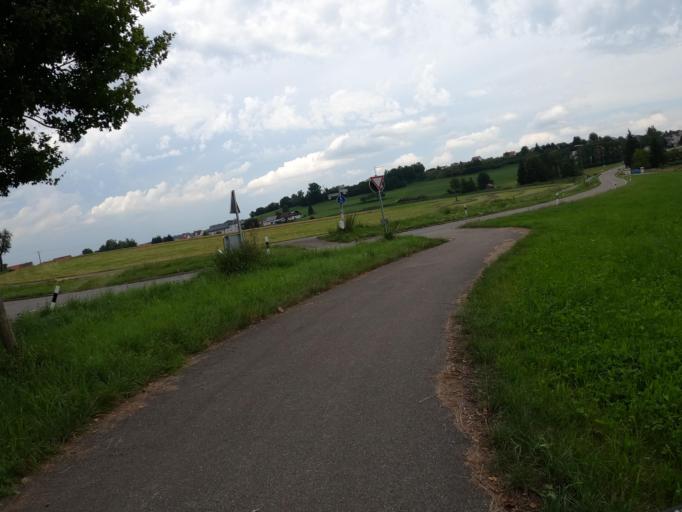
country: DE
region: Bavaria
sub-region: Swabia
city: Pfaffenhofen an der Roth
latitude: 48.3961
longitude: 10.1888
